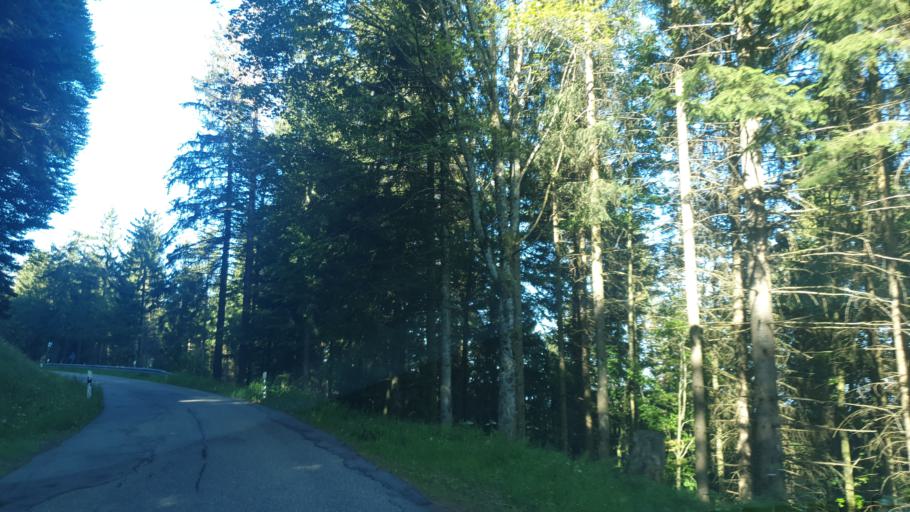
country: DE
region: Baden-Wuerttemberg
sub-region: Freiburg Region
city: Horben
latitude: 47.9027
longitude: 7.8681
